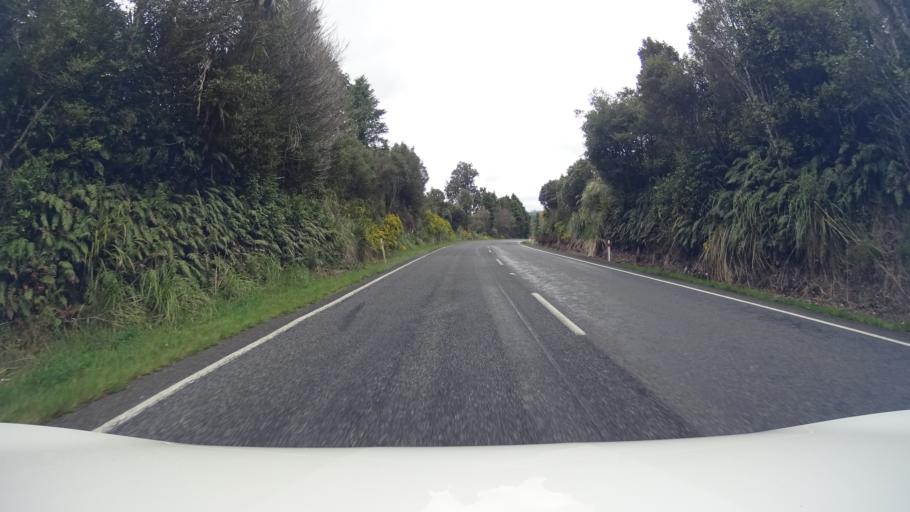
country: NZ
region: Manawatu-Wanganui
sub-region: Ruapehu District
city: Waiouru
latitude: -39.2371
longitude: 175.3916
